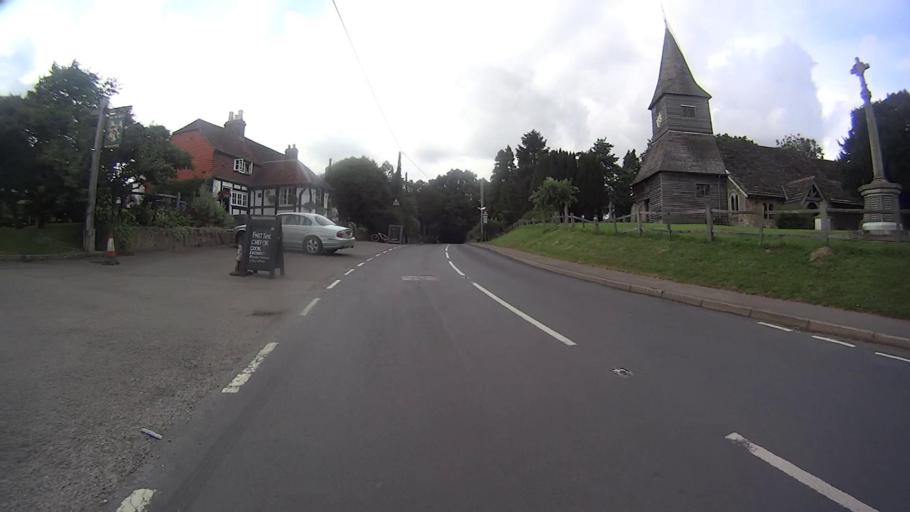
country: GB
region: England
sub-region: Surrey
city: Newdigate
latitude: 51.1650
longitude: -0.2888
